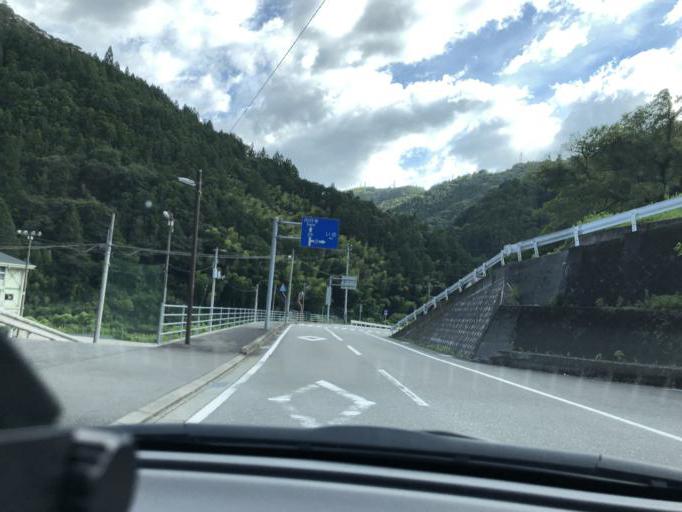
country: JP
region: Kochi
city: Kochi-shi
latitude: 33.6236
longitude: 133.4981
